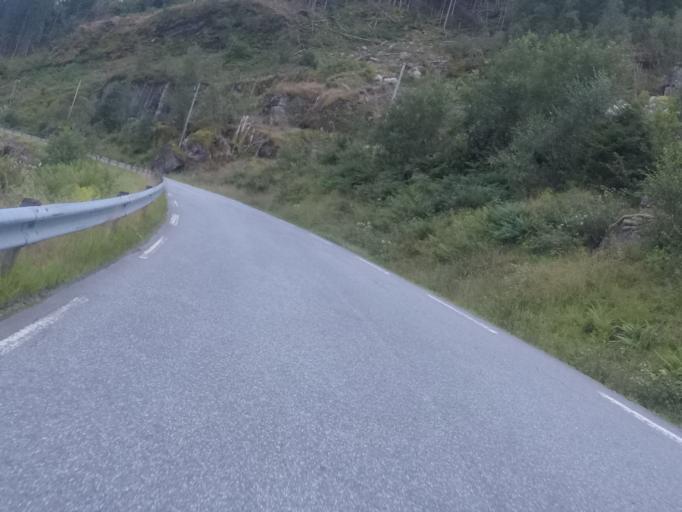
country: NO
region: Sogn og Fjordane
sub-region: Balestrand
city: Balestrand
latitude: 61.2757
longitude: 6.4999
